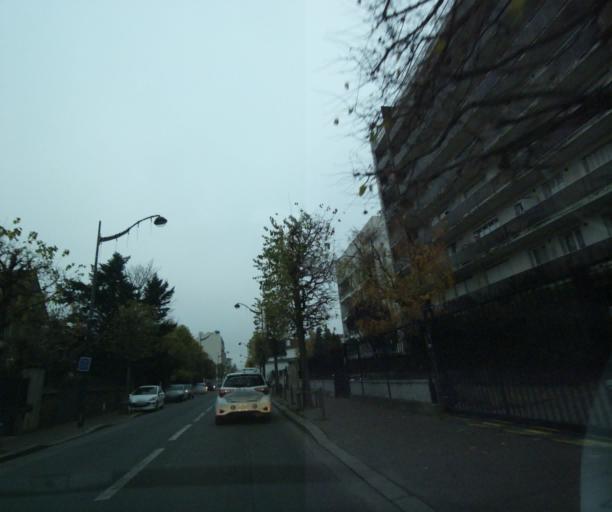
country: FR
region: Ile-de-France
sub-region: Departement de Seine-Saint-Denis
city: Les Pavillons-sous-Bois
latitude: 48.9051
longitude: 2.5025
